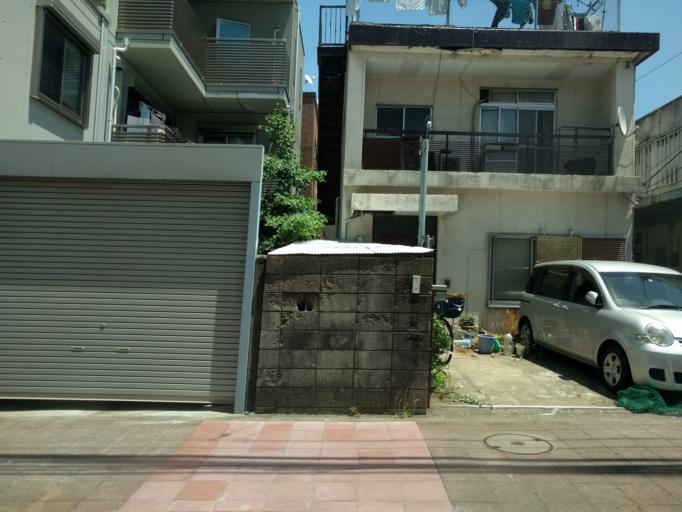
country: JP
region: Tokyo
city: Mitaka-shi
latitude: 35.6626
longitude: 139.6031
